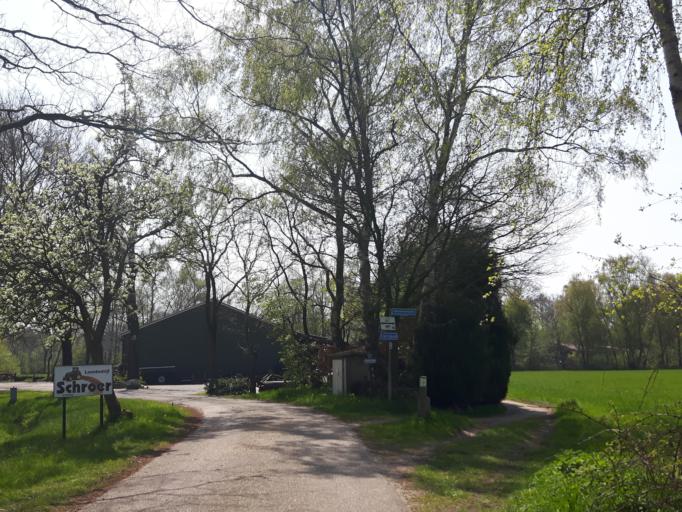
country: DE
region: North Rhine-Westphalia
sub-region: Regierungsbezirk Munster
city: Vreden
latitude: 52.1195
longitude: 6.8276
